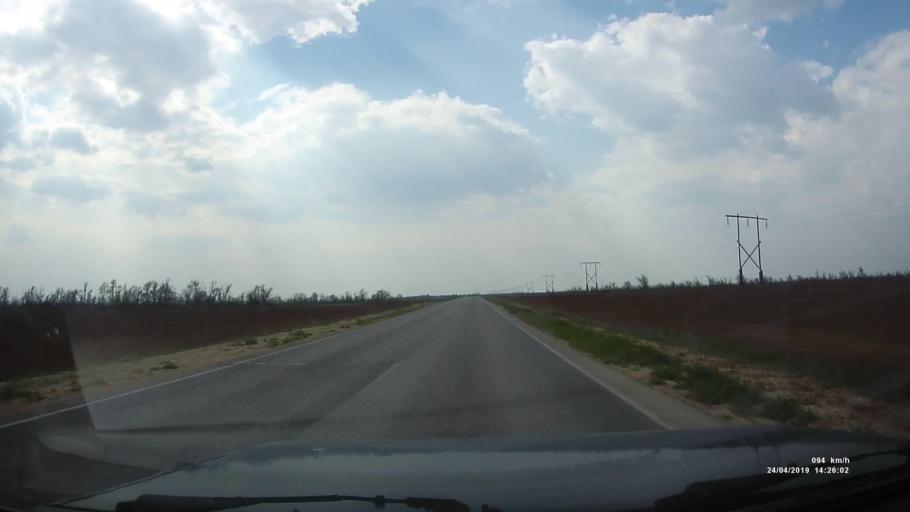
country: RU
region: Kalmykiya
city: Arshan'
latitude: 46.3325
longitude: 44.0705
